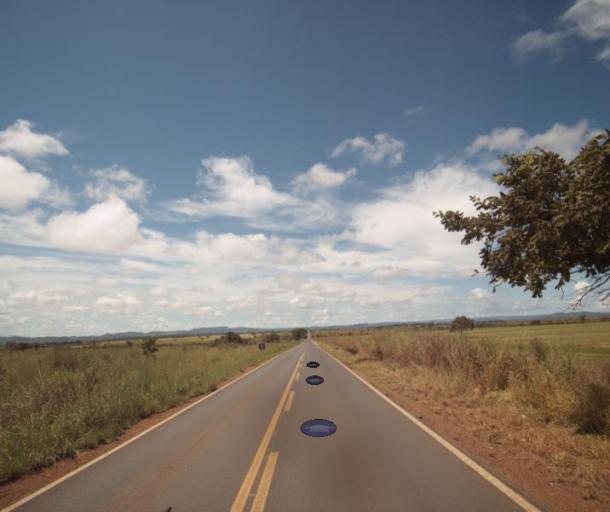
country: BR
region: Goias
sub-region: Padre Bernardo
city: Padre Bernardo
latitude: -15.2811
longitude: -48.2577
